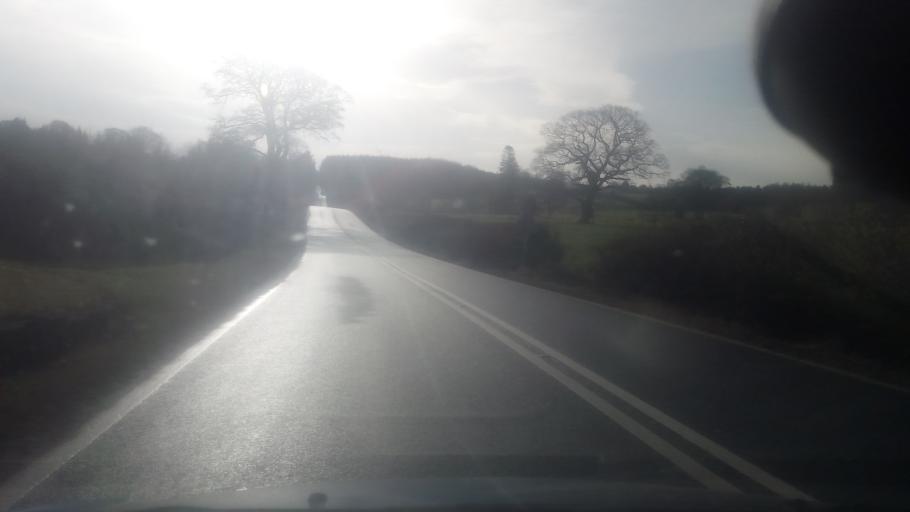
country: GB
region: Scotland
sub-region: The Scottish Borders
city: Jedburgh
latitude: 55.4533
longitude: -2.5564
